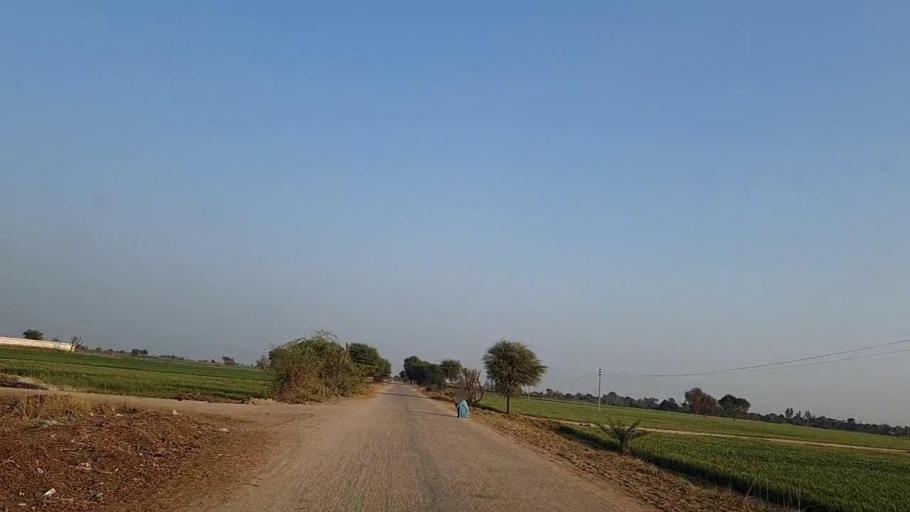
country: PK
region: Sindh
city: Sakrand
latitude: 26.0435
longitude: 68.4228
